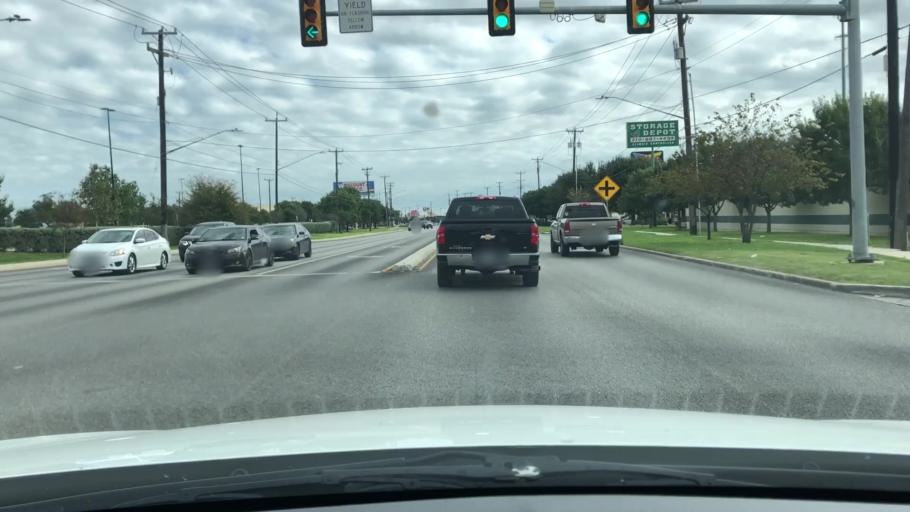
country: US
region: Texas
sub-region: Bexar County
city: Leon Valley
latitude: 29.4867
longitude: -98.6703
